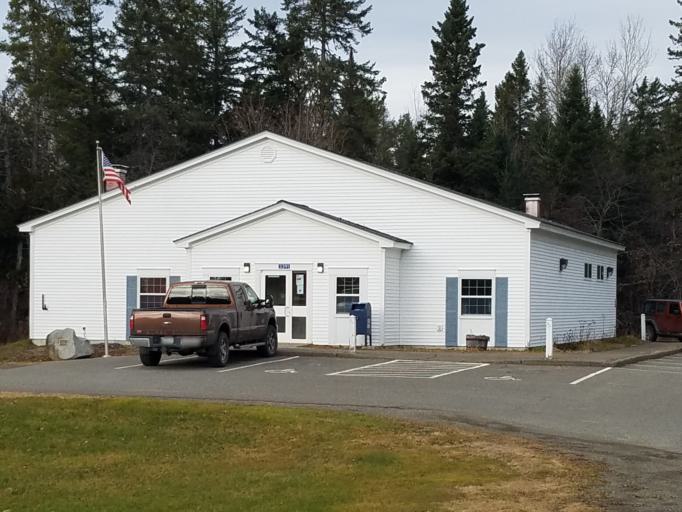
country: US
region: Maine
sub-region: Aroostook County
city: Hodgdon
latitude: 46.1312
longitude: -68.1616
